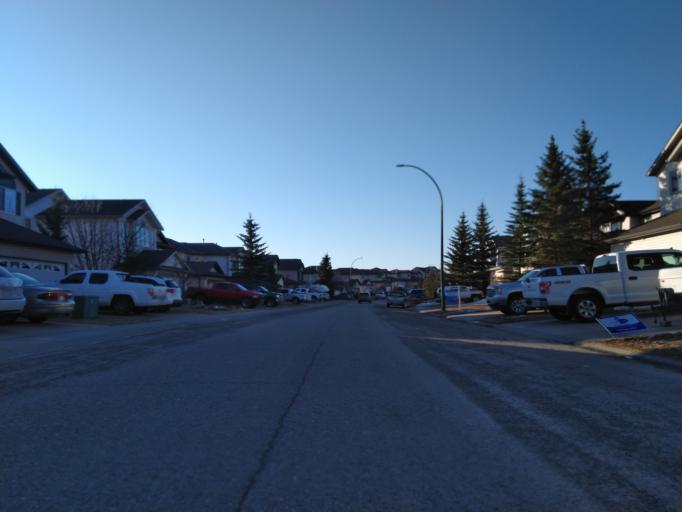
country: CA
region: Alberta
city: Cochrane
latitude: 51.1855
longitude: -114.5103
